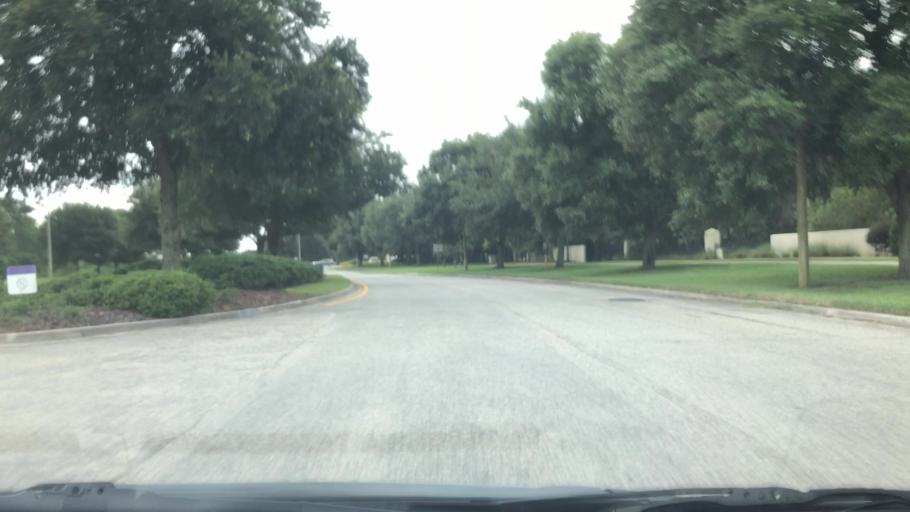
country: US
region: Florida
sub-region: Saint Johns County
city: Fruit Cove
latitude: 30.1380
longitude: -81.5475
